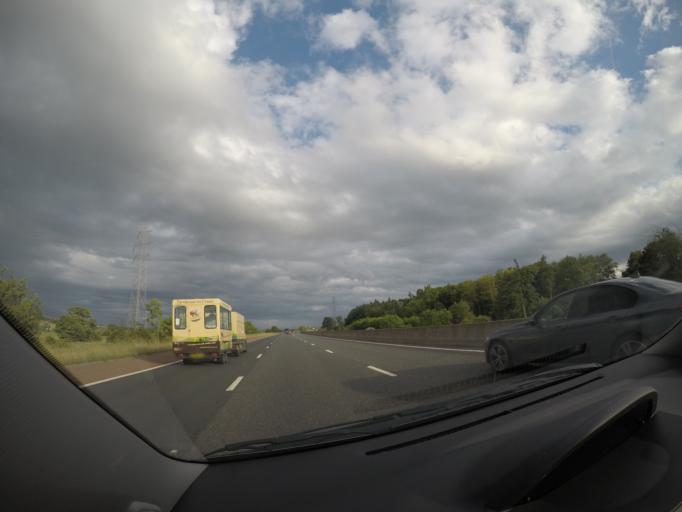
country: GB
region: England
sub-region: Cumbria
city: Penrith
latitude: 54.6768
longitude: -2.7804
